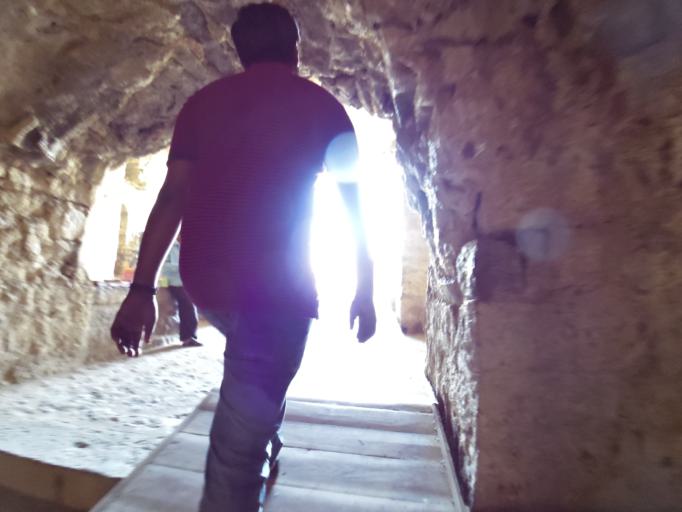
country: IN
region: Telangana
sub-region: Hyderabad
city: Hyderabad
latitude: 17.3823
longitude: 78.4020
